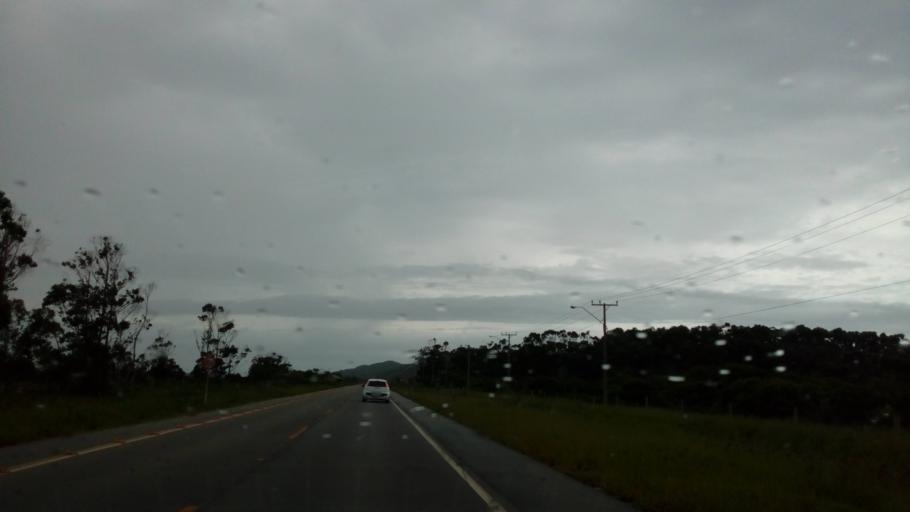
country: BR
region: Santa Catarina
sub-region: Laguna
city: Laguna
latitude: -28.5340
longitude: -48.7833
